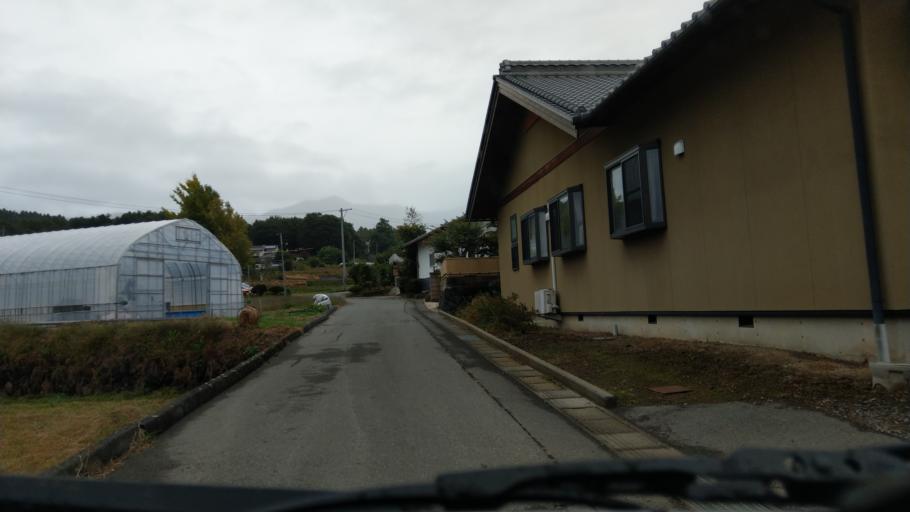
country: JP
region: Nagano
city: Komoro
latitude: 36.3338
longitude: 138.4512
